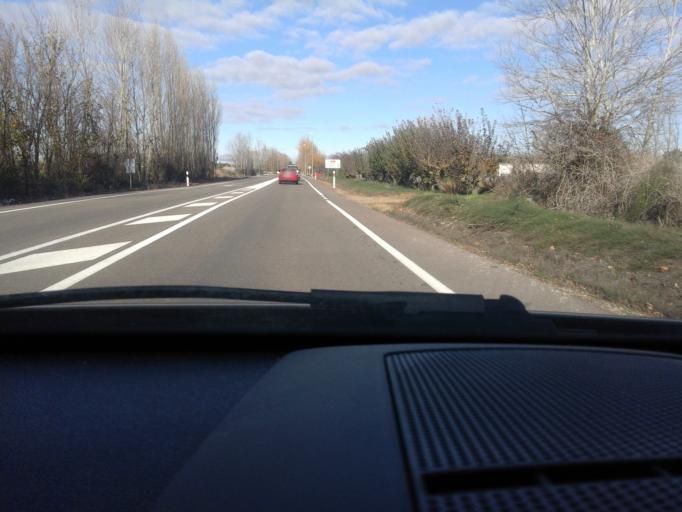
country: ES
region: Castille and Leon
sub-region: Provincia de Palencia
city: Carrion de los Condes
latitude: 42.3450
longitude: -4.6173
